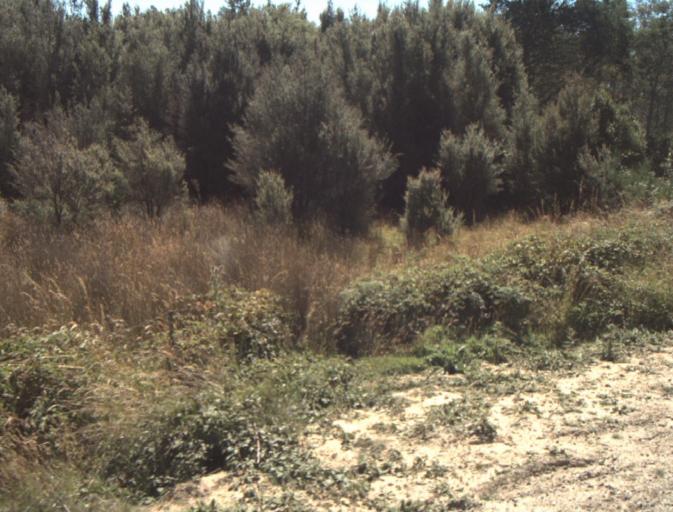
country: AU
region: Tasmania
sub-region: Dorset
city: Scottsdale
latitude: -41.3402
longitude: 147.4308
